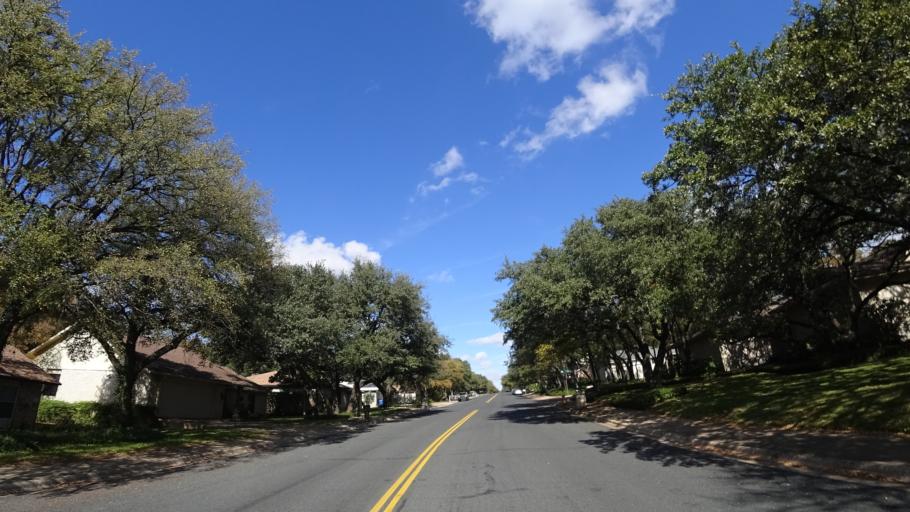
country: US
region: Texas
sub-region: Williamson County
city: Jollyville
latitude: 30.4163
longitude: -97.7281
